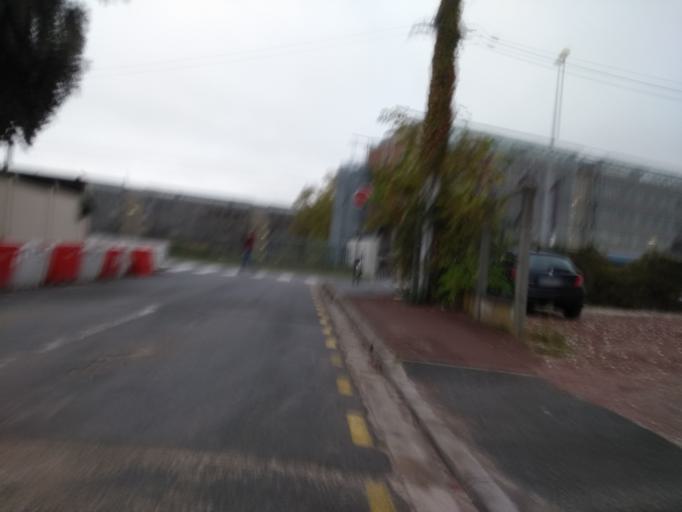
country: FR
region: Aquitaine
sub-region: Departement de la Gironde
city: Talence
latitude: 44.8057
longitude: -0.5985
